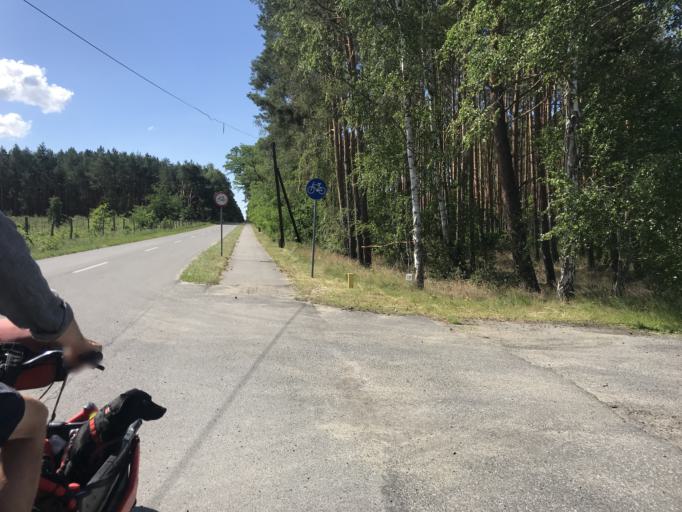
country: PL
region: Lubusz
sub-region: Powiat krosnienski
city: Gubin
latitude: 52.0572
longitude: 14.7625
